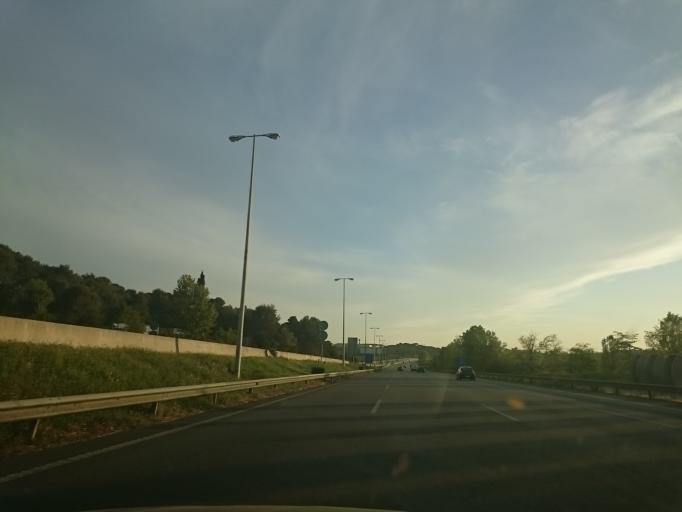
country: ES
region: Catalonia
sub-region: Provincia de Barcelona
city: Granollers
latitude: 41.5890
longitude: 2.3050
